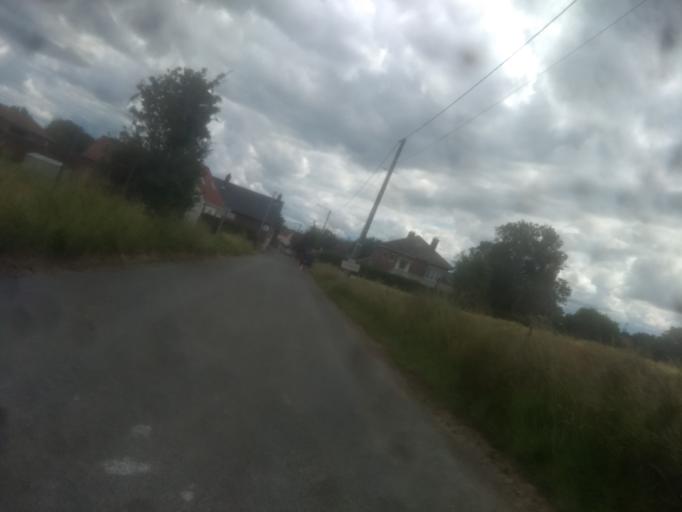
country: FR
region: Nord-Pas-de-Calais
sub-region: Departement du Pas-de-Calais
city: Agny
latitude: 50.2289
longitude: 2.7366
